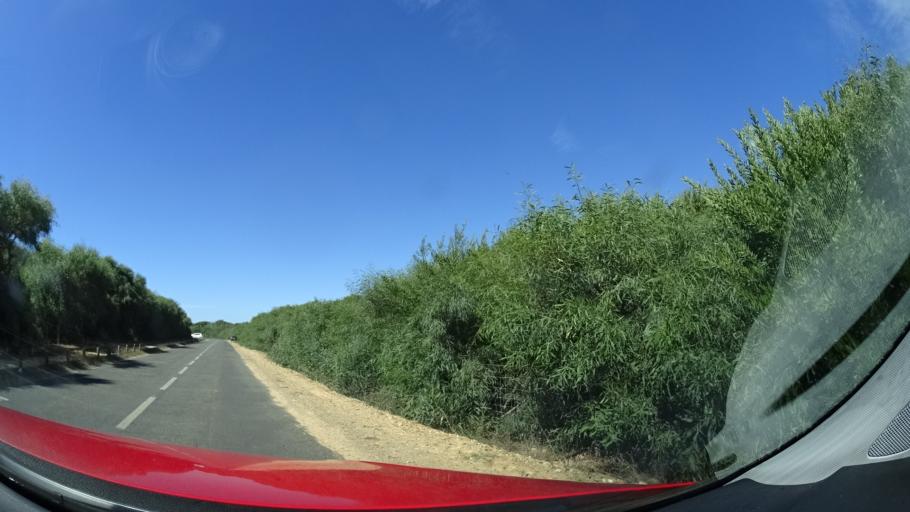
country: PT
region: Beja
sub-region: Odemira
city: Sao Teotonio
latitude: 37.5347
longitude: -8.7846
